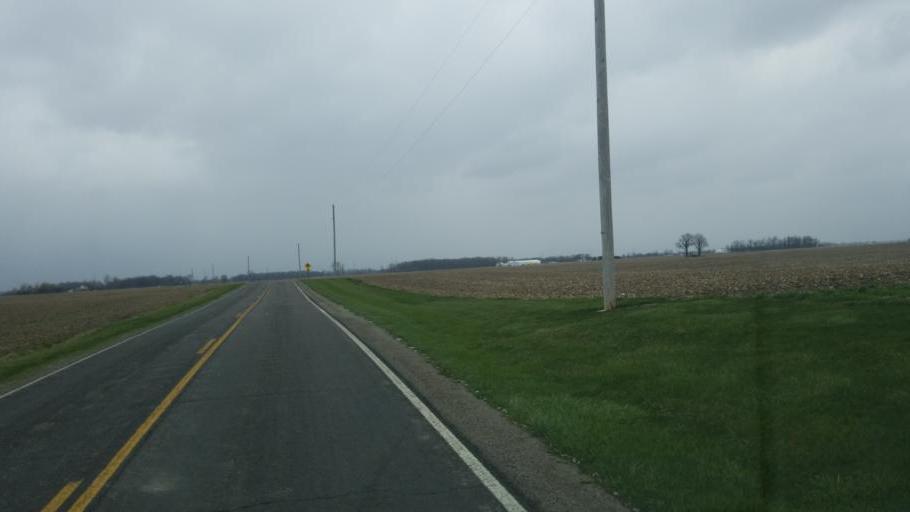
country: US
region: Ohio
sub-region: Union County
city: Richwood
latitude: 40.4412
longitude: -83.3938
